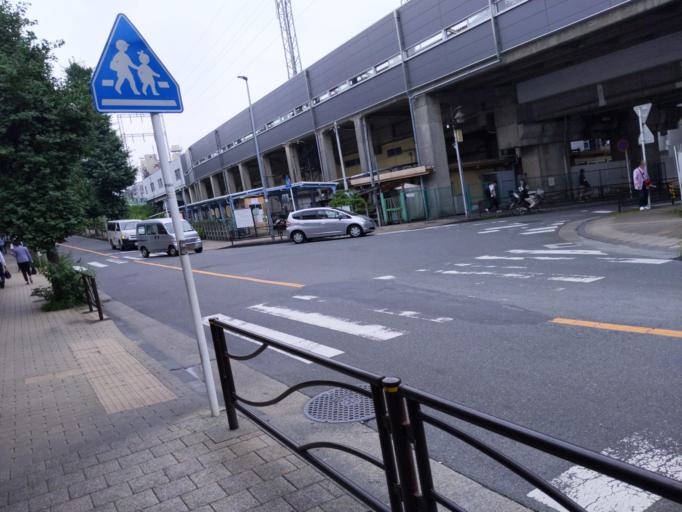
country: JP
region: Tokyo
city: Chofugaoka
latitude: 35.5852
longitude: 139.5826
